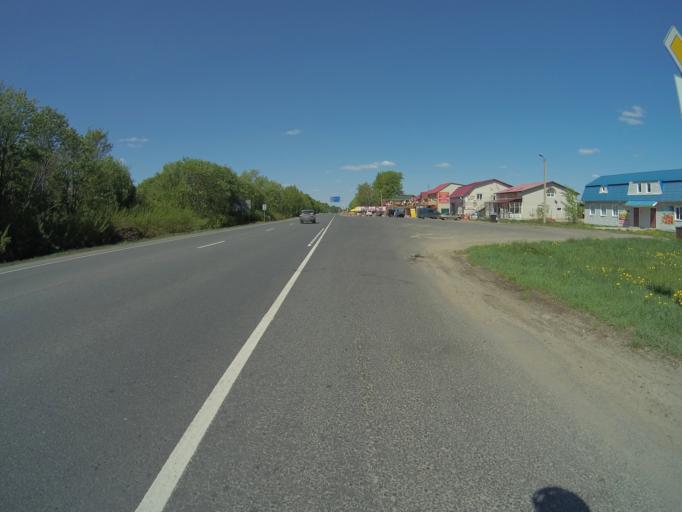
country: RU
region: Vladimir
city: Suzdal'
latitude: 56.3813
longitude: 40.4563
